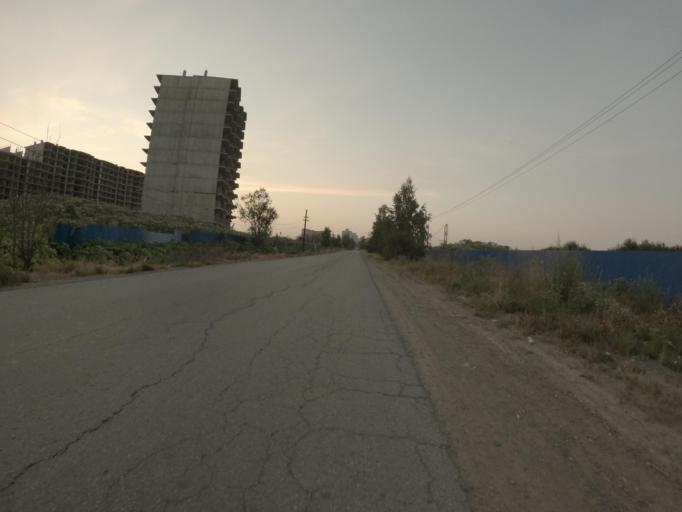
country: RU
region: Leningrad
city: Yanino Vtoroye
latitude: 59.9423
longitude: 30.5534
